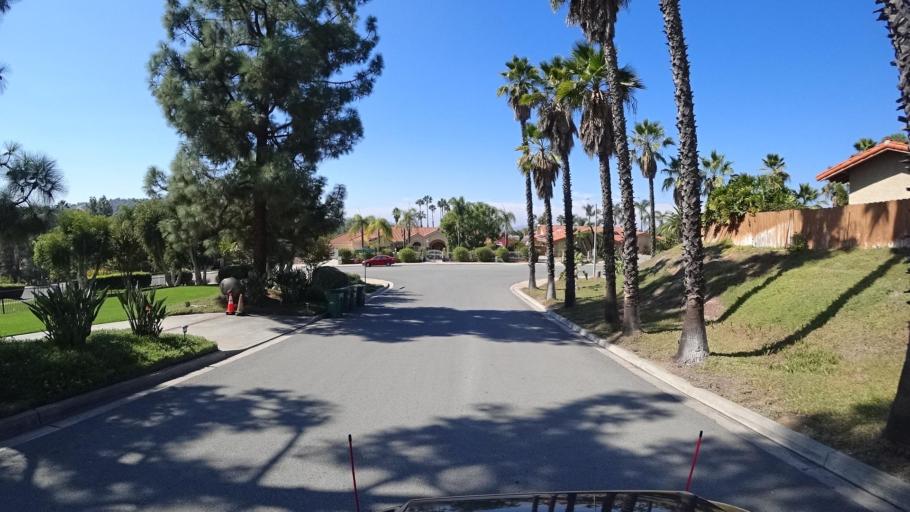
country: US
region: California
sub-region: San Diego County
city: Granite Hills
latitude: 32.7855
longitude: -116.9004
